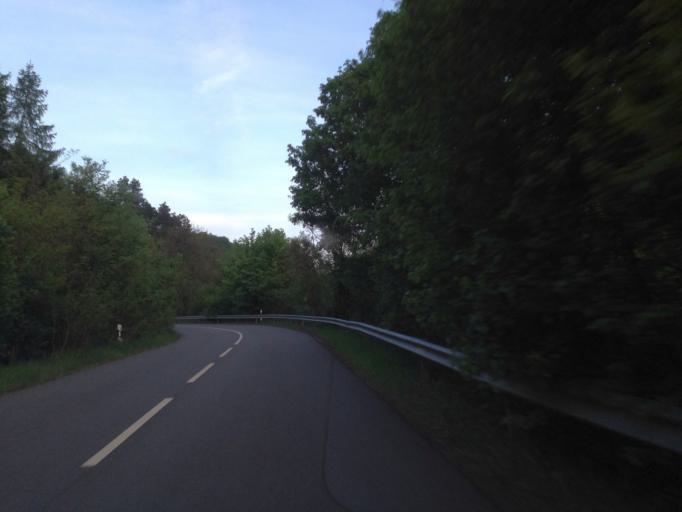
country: HU
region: Nograd
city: Batonyterenye
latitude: 47.8980
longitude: 19.8198
